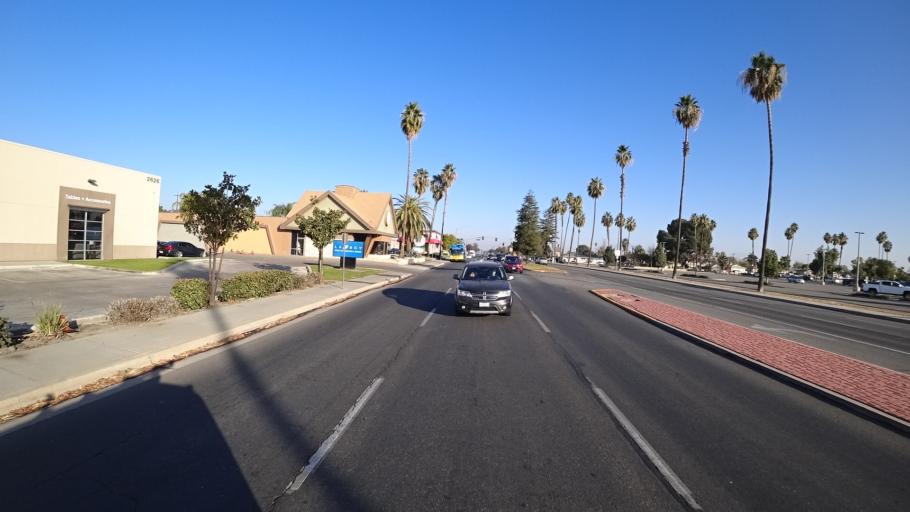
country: US
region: California
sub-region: Kern County
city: Bakersfield
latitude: 35.3396
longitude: -119.0316
